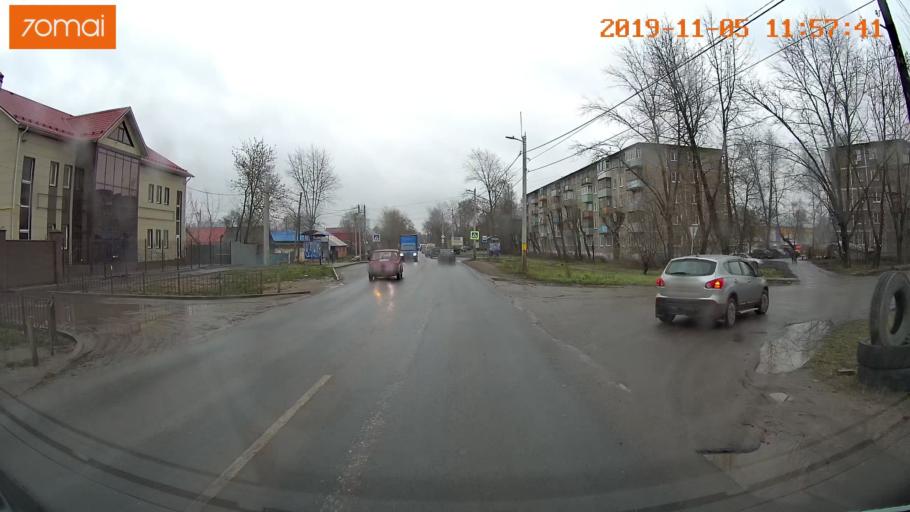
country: RU
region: Ivanovo
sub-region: Gorod Ivanovo
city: Ivanovo
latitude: 56.9826
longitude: 41.0357
